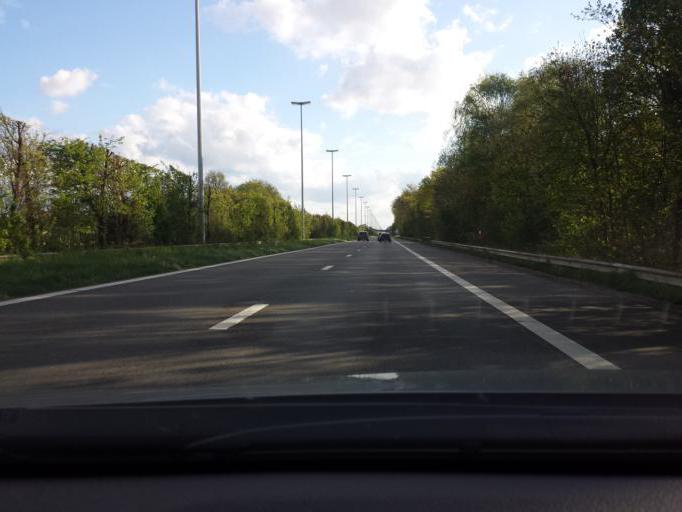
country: BE
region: Wallonia
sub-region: Province de Liege
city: Lontzen
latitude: 50.6759
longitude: 6.0398
